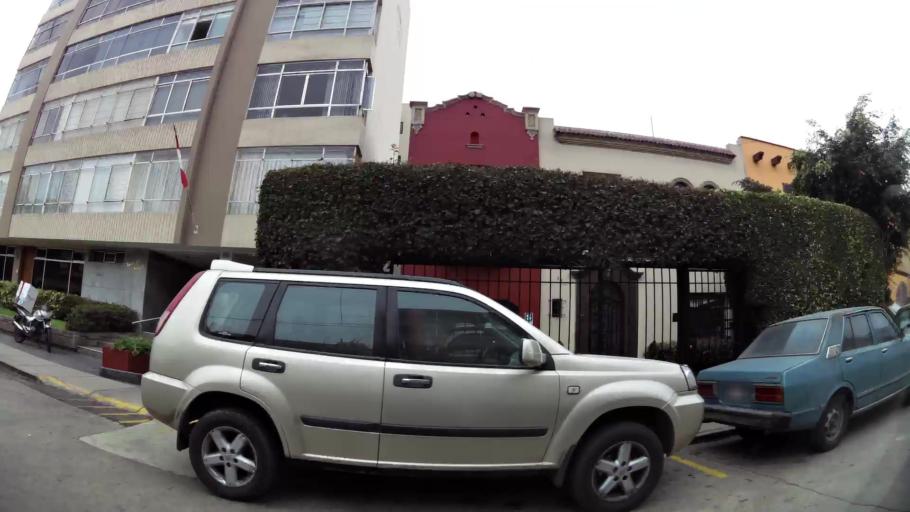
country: PE
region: Lima
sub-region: Lima
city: San Isidro
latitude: -12.0896
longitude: -77.0507
